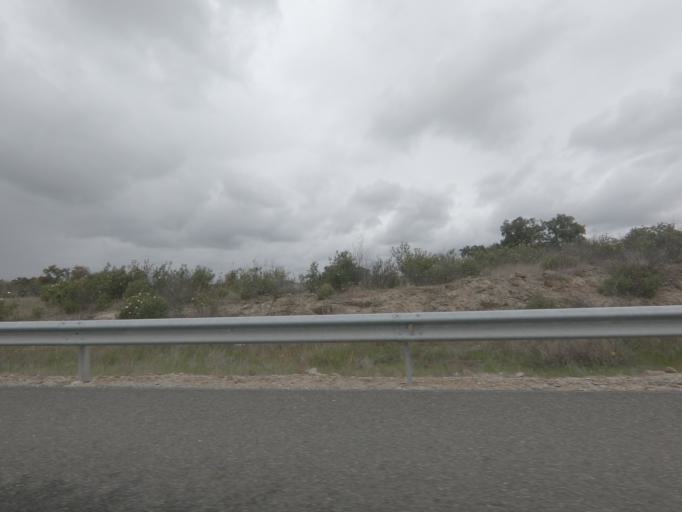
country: ES
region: Extremadura
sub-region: Provincia de Caceres
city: Segura de Toro
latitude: 40.2480
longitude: -5.9525
